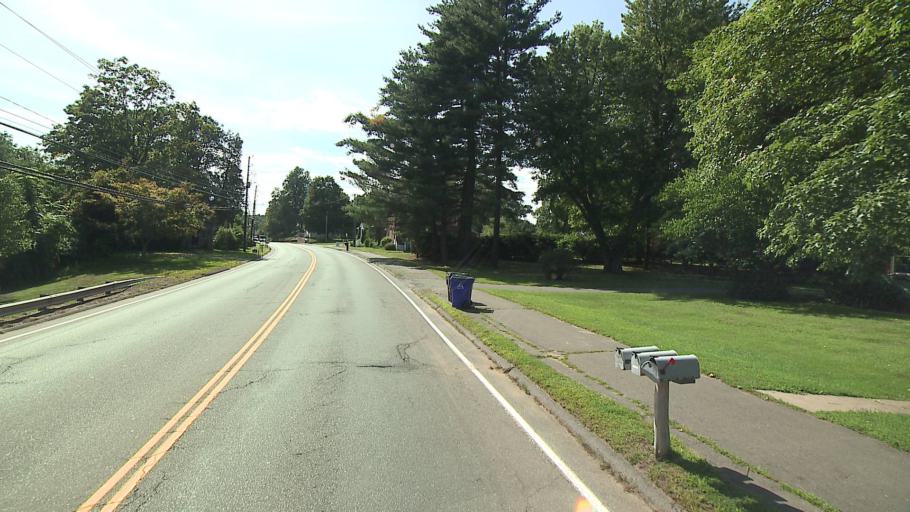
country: US
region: Connecticut
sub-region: Hartford County
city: Simsbury Center
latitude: 41.8708
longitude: -72.8091
